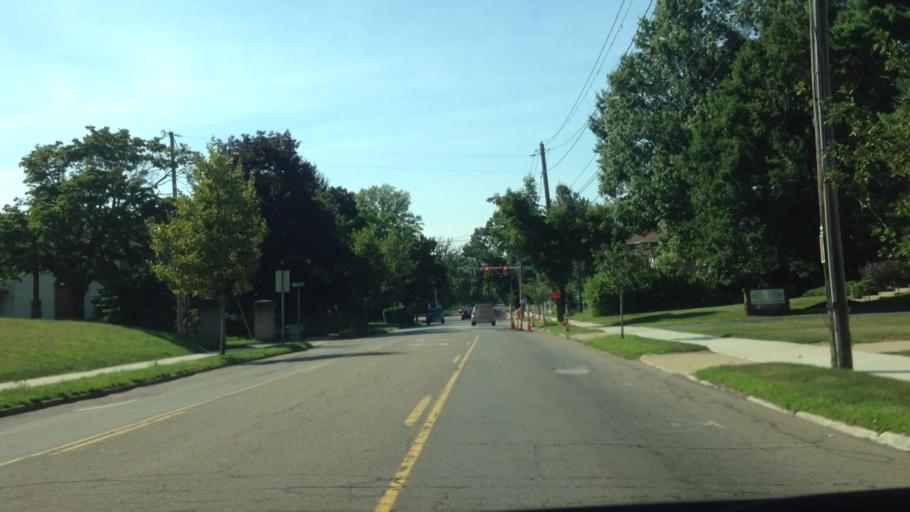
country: US
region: Ohio
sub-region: Summit County
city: Akron
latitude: 41.0982
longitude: -81.5470
